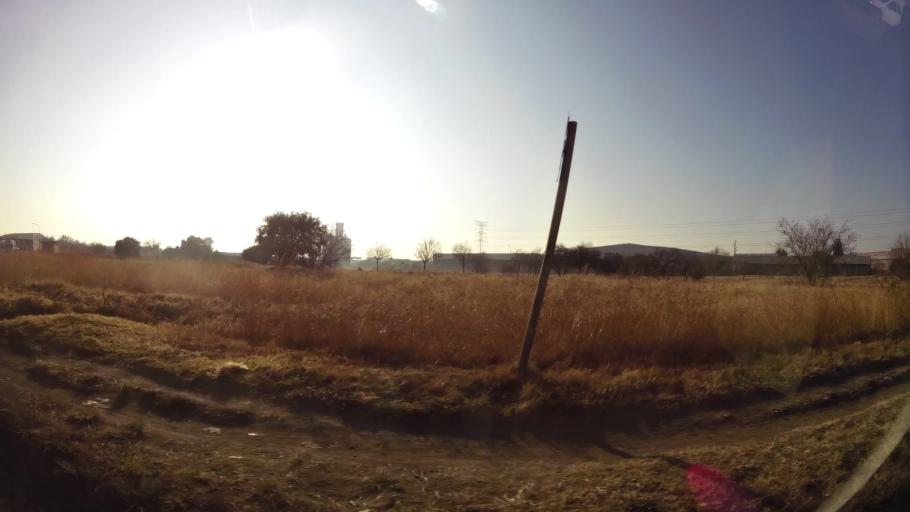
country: ZA
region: Orange Free State
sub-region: Mangaung Metropolitan Municipality
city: Bloemfontein
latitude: -29.1652
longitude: 26.2203
